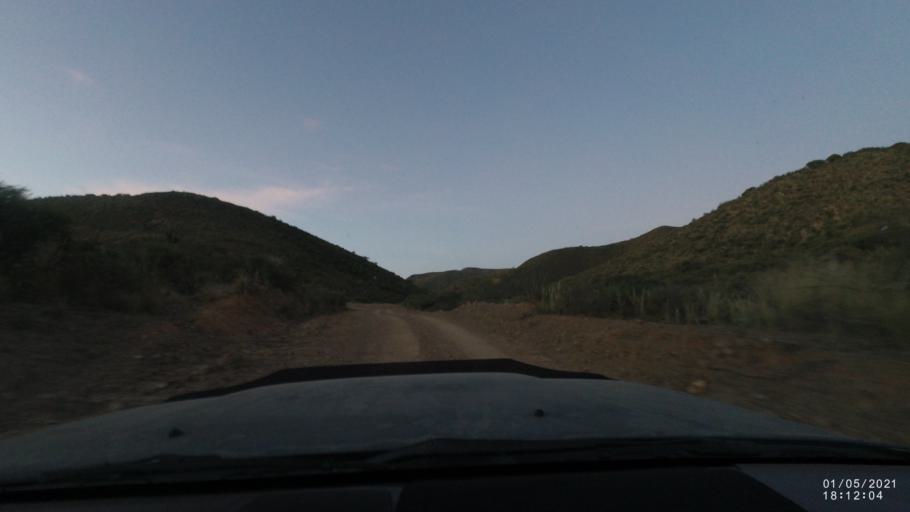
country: BO
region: Cochabamba
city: Capinota
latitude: -17.6790
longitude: -66.2010
